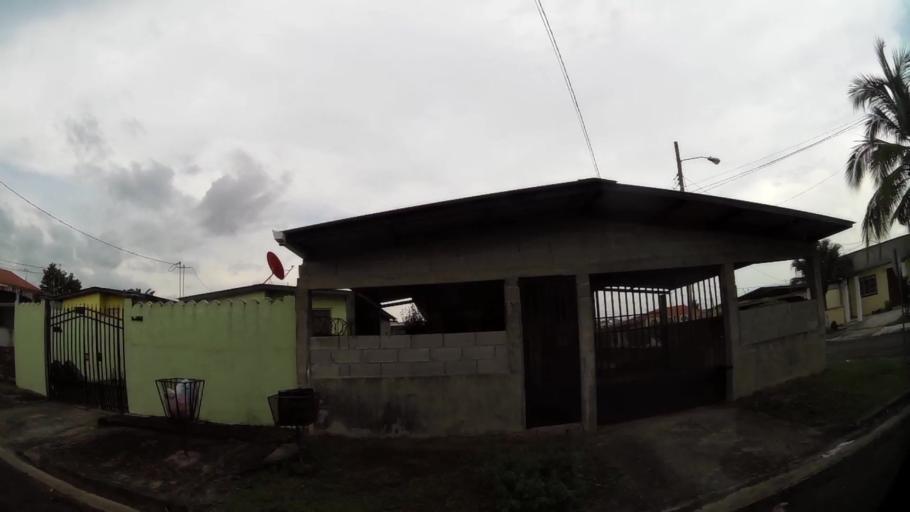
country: PA
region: Panama
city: Cabra Numero Uno
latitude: 9.0945
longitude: -79.3456
